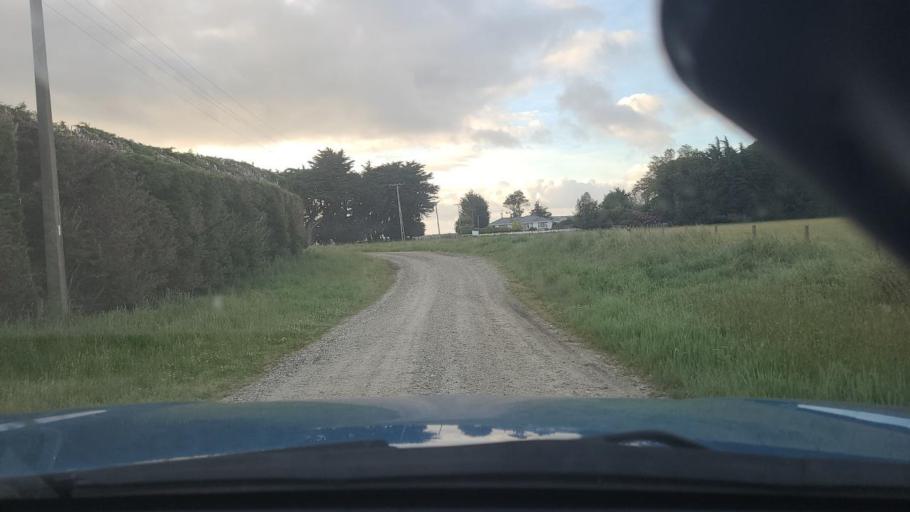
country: NZ
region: Southland
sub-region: Invercargill City
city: Invercargill
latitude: -46.4812
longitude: 168.7138
